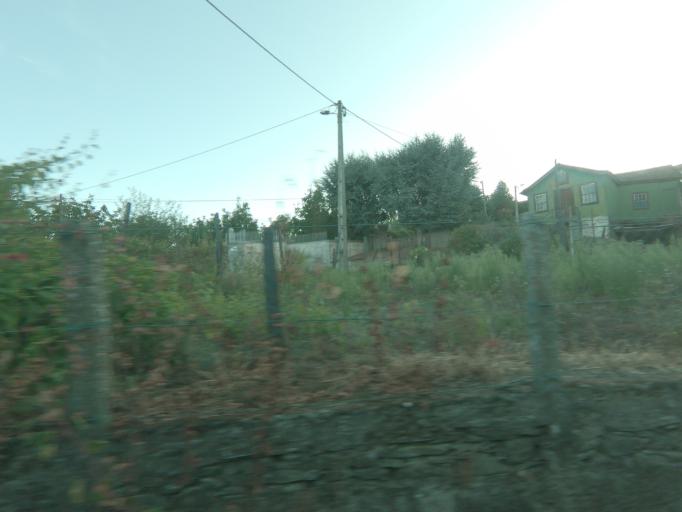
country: PT
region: Vila Real
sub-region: Mesao Frio
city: Mesao Frio
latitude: 41.1898
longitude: -7.8596
